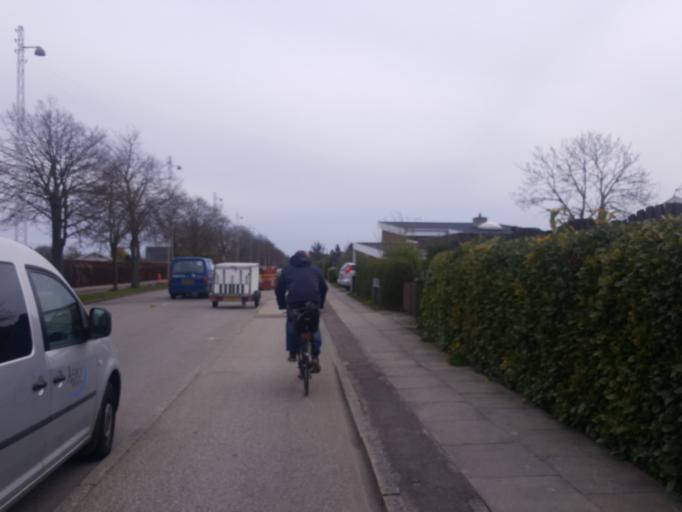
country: DK
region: Capital Region
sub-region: Tarnby Kommune
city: Tarnby
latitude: 55.6211
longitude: 12.5921
